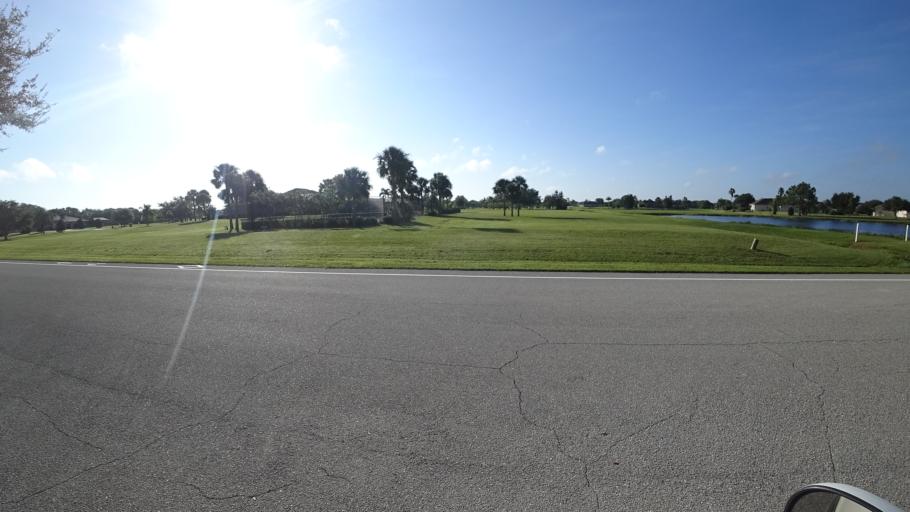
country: US
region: Florida
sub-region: Hillsborough County
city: Sun City Center
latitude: 27.5598
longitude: -82.3590
